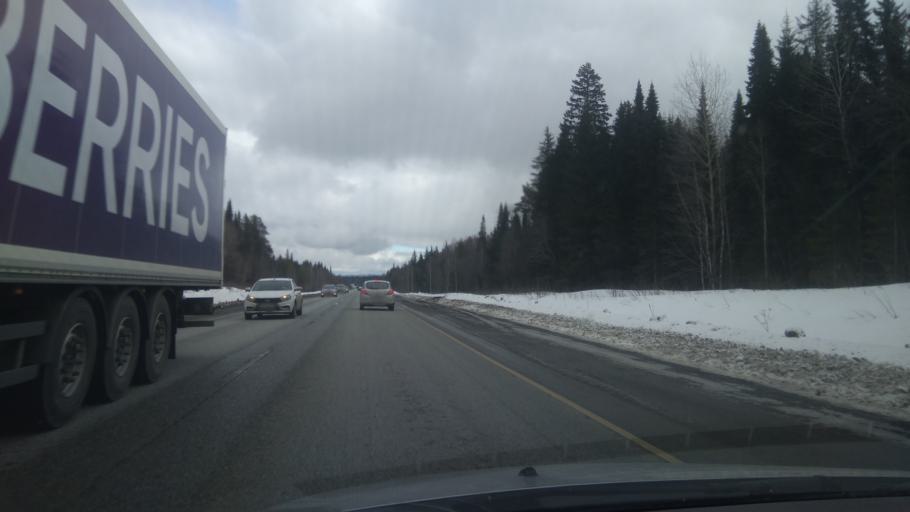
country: RU
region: Sverdlovsk
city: Druzhinino
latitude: 56.7963
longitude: 59.4233
